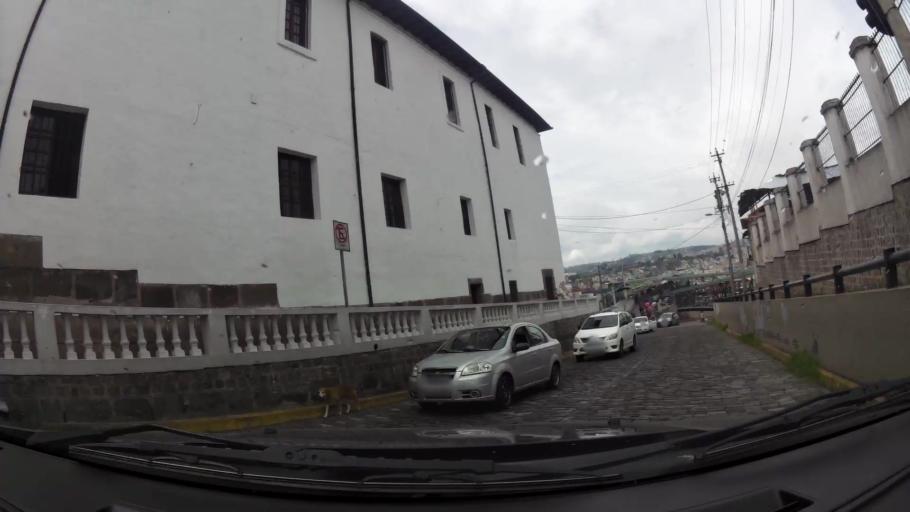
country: EC
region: Pichincha
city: Quito
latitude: -0.2143
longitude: -78.5173
